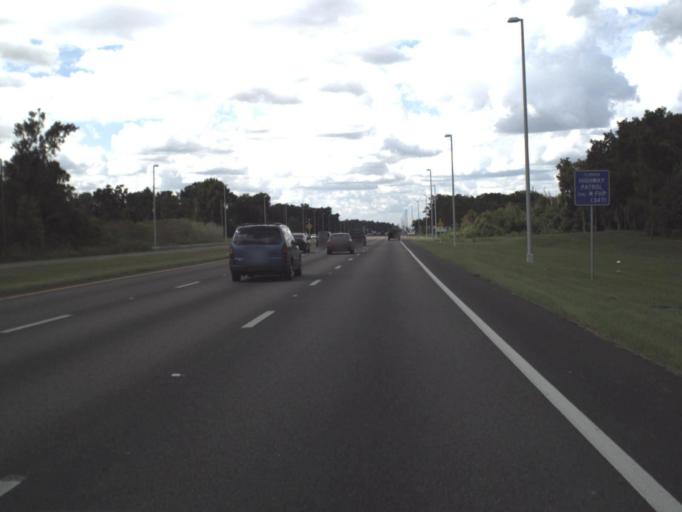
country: US
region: Florida
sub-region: Polk County
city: Bartow
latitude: 27.9150
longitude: -81.8451
